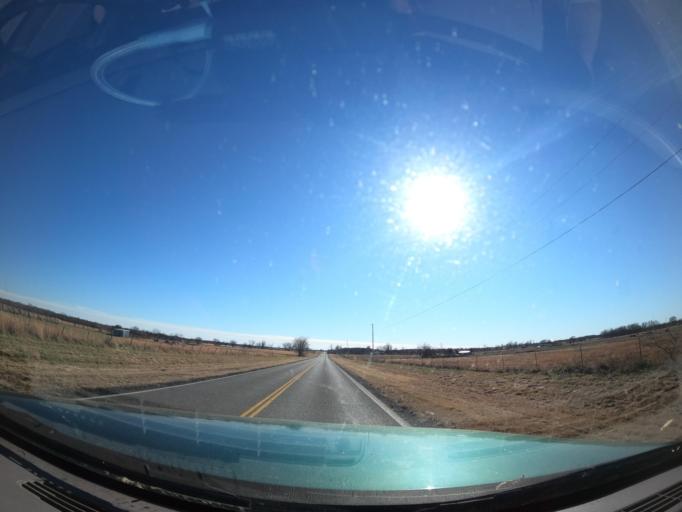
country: US
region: Oklahoma
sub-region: Muskogee County
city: Haskell
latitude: 35.6853
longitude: -95.6423
